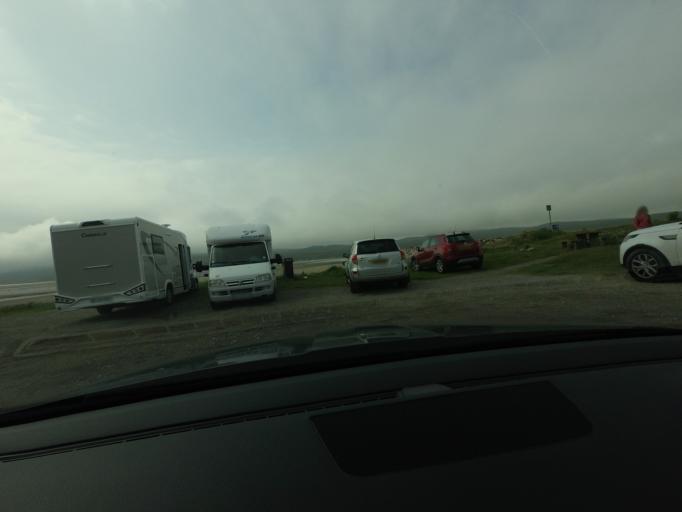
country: GB
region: Scotland
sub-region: Highland
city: Golspie
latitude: 58.4919
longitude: -4.4361
